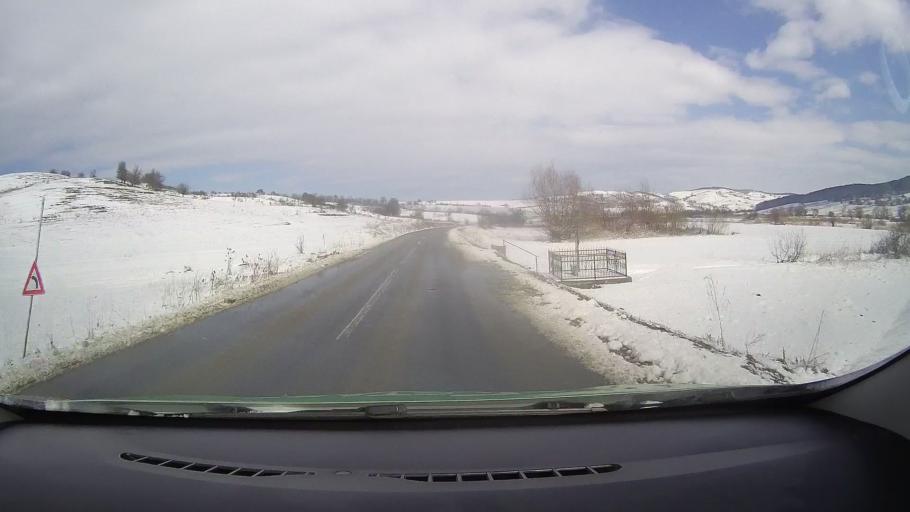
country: RO
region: Sibiu
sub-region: Comuna Altina
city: Altina
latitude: 45.9574
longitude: 24.4542
